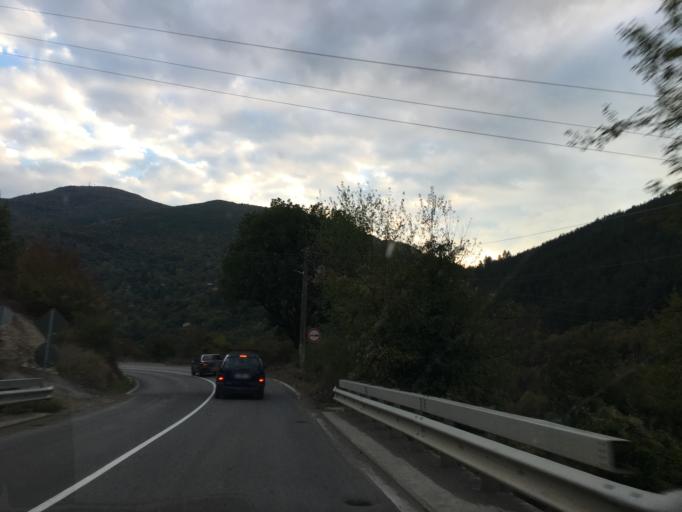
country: BG
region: Sofiya
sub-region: Obshtina Svoge
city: Svoge
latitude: 42.9175
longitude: 23.3862
